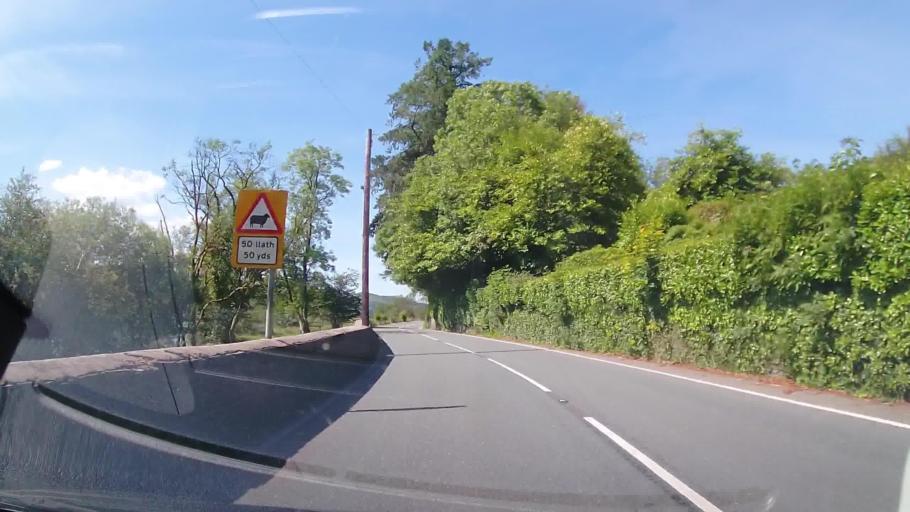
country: GB
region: Wales
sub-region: Sir Powys
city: Machynlleth
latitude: 52.5997
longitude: -3.8613
